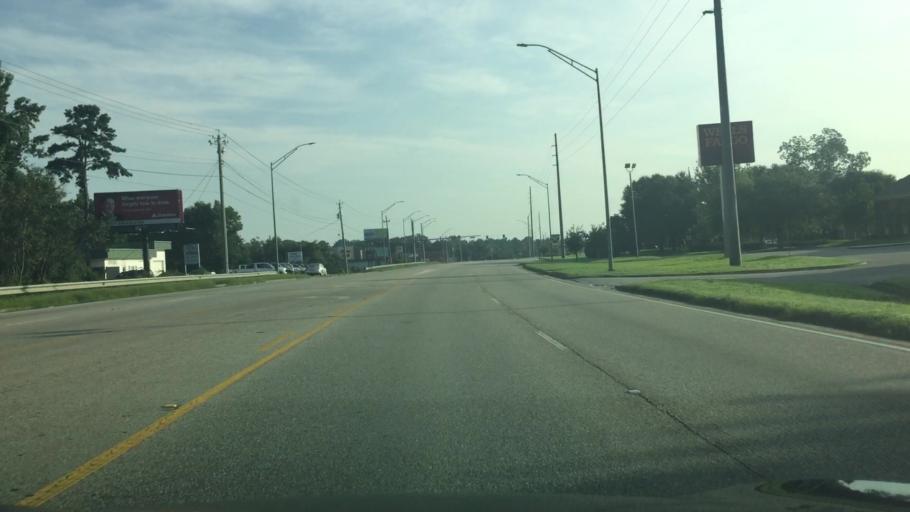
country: US
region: Alabama
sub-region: Covington County
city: Andalusia
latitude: 31.3144
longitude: -86.4990
